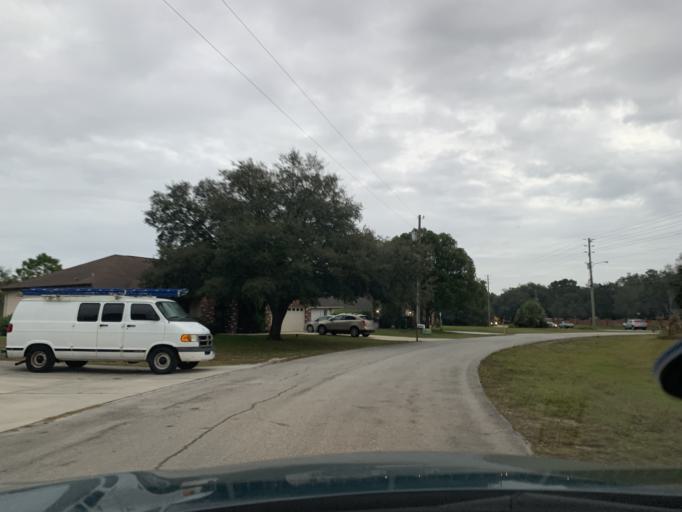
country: US
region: Florida
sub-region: Hernando County
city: Timber Pines
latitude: 28.4343
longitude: -82.5894
